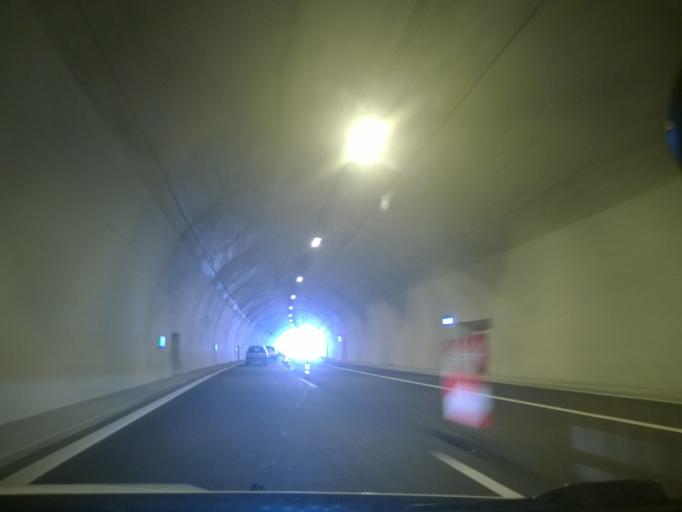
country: GR
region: West Greece
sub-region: Nomos Achaias
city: Aiyira
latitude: 38.1310
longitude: 22.4322
